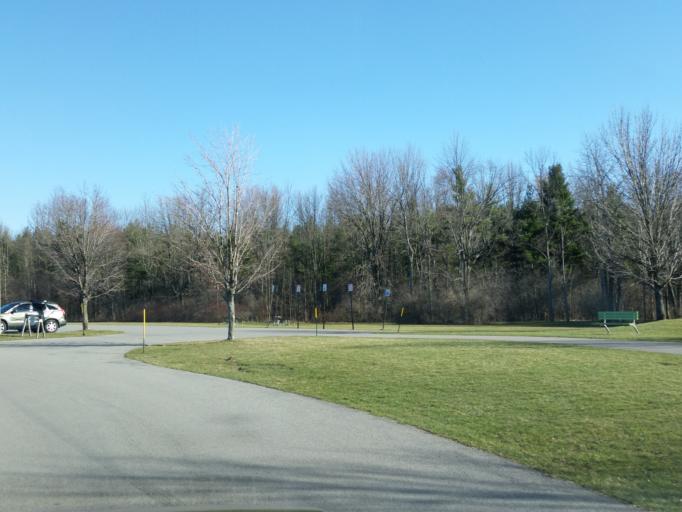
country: US
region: New York
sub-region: Monroe County
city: Scottsville
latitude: 43.0812
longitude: -77.8010
